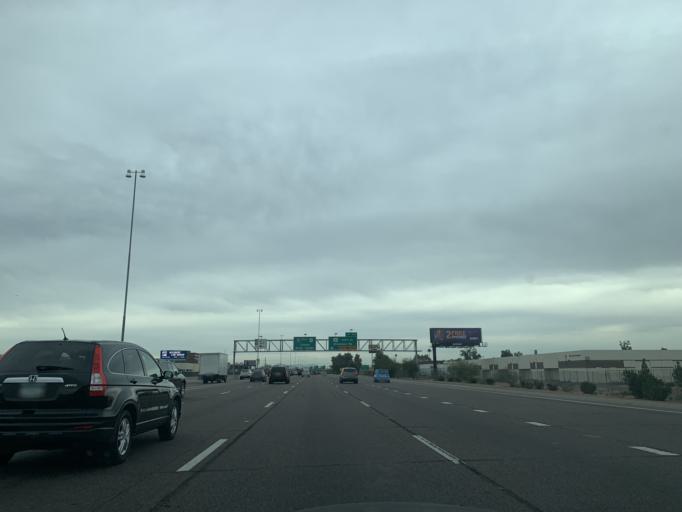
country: US
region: Arizona
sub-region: Maricopa County
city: Tempe Junction
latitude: 33.4105
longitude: -111.9898
